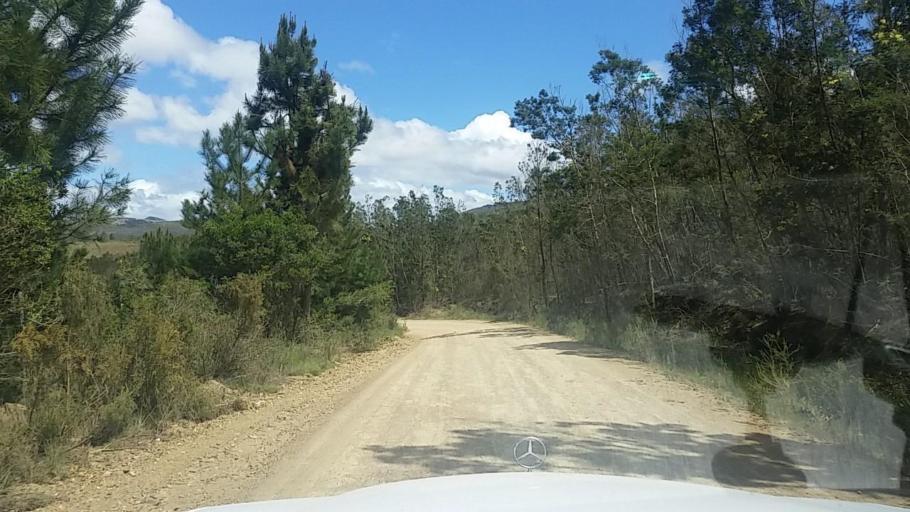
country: ZA
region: Western Cape
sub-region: Eden District Municipality
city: Knysna
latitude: -33.8575
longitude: 23.1875
